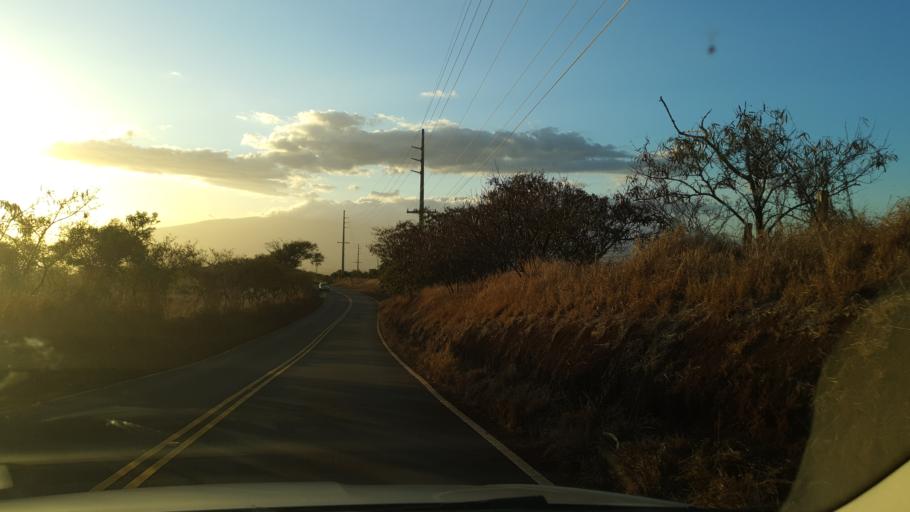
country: US
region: Hawaii
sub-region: Maui County
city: Pukalani
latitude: 20.7900
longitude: -156.3543
